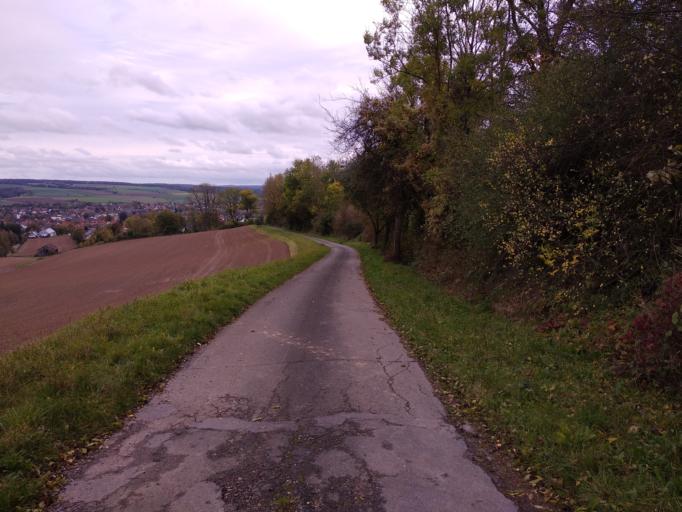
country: DE
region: North Rhine-Westphalia
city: Beverungen
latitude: 51.6644
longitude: 9.3532
